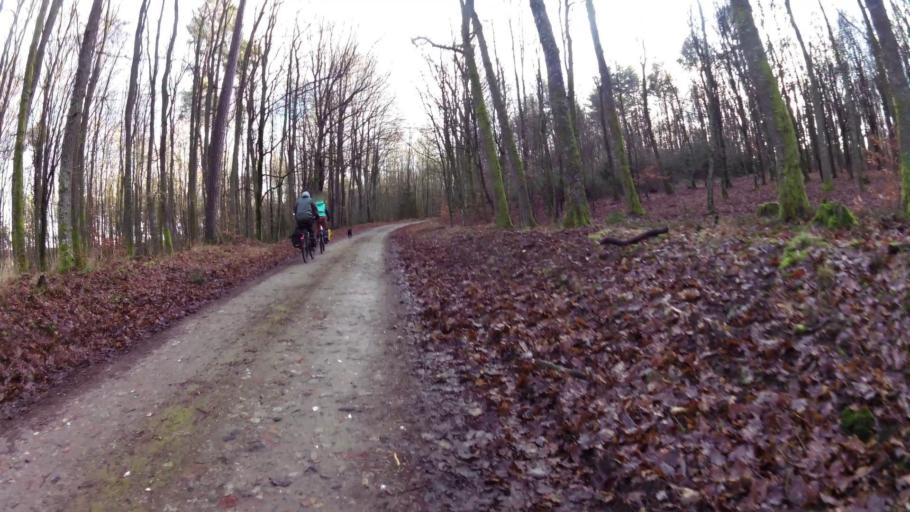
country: PL
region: West Pomeranian Voivodeship
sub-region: Powiat koszalinski
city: Sianow
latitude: 54.1137
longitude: 16.2976
